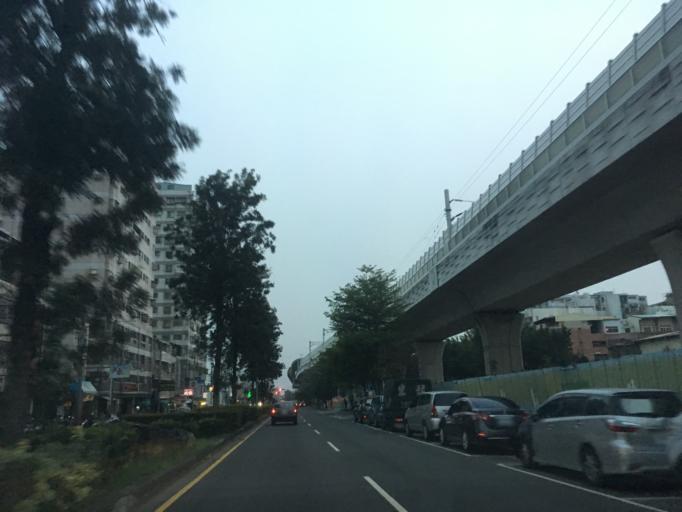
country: TW
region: Taiwan
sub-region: Taichung City
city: Taichung
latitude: 24.1674
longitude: 120.7005
